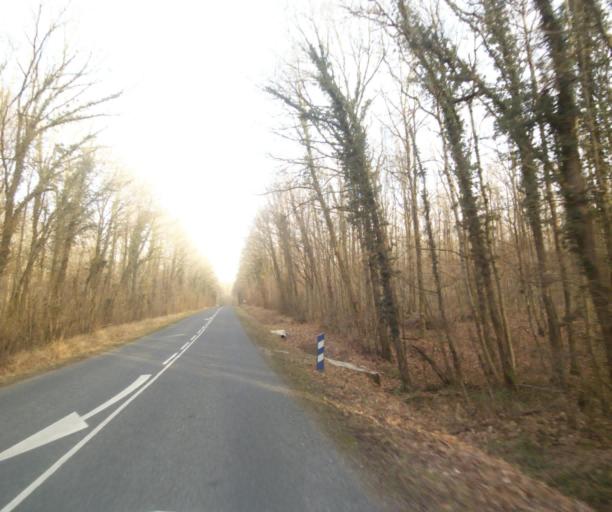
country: FR
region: Champagne-Ardenne
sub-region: Departement de la Haute-Marne
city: Bettancourt-la-Ferree
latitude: 48.6765
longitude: 4.9418
